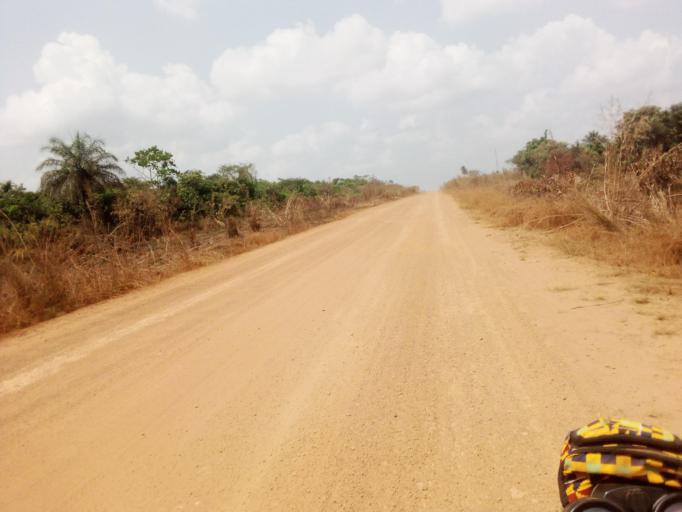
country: SL
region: Southern Province
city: Mogbwemo
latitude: 7.6605
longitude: -12.2668
